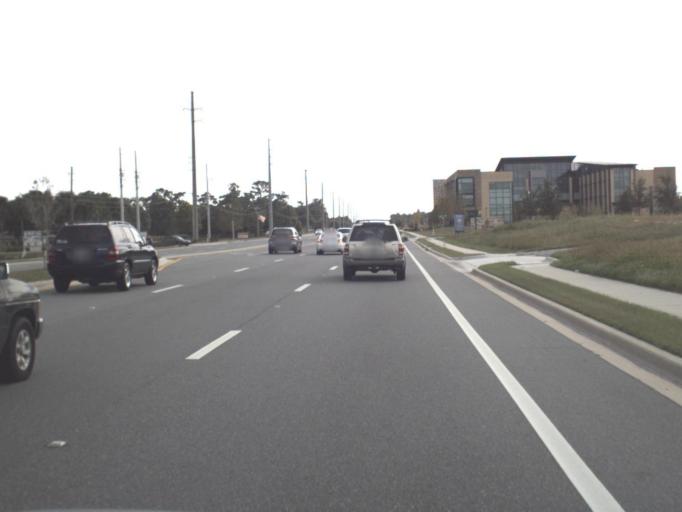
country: US
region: Florida
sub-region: Osceola County
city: Buenaventura Lakes
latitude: 28.3875
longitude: -81.2445
